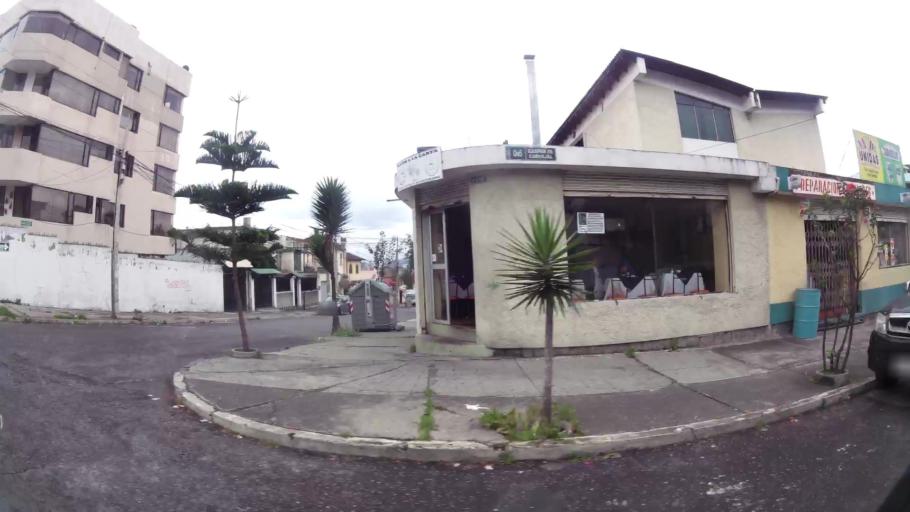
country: EC
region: Pichincha
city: Quito
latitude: -0.1924
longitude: -78.5004
